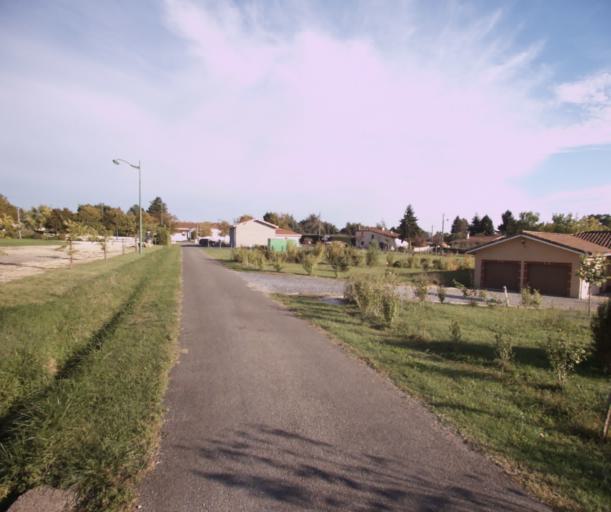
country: FR
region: Midi-Pyrenees
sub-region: Departement du Gers
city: Eauze
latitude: 43.8637
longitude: 0.0255
